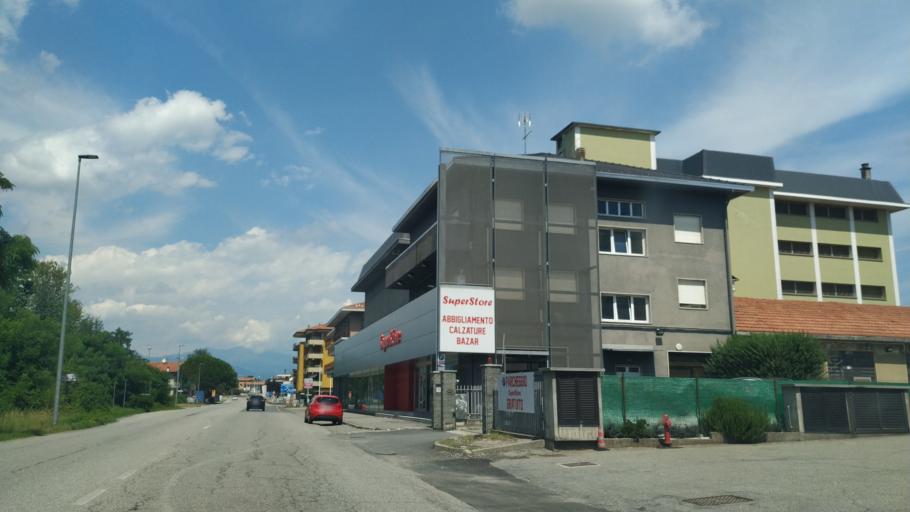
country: IT
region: Piedmont
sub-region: Provincia di Novara
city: Briga Novarese
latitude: 45.7151
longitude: 8.4519
